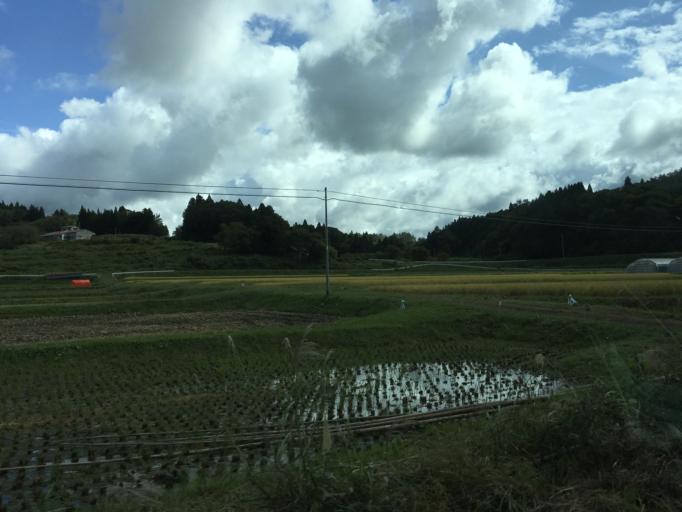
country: JP
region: Iwate
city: Ichinoseki
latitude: 38.8468
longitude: 141.3401
